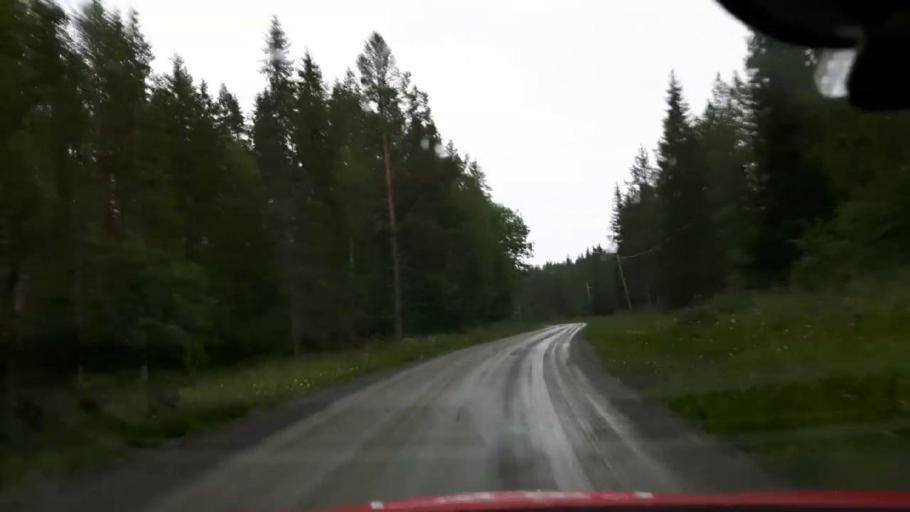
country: SE
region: Jaemtland
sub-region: OEstersunds Kommun
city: Brunflo
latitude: 62.8964
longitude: 14.8685
